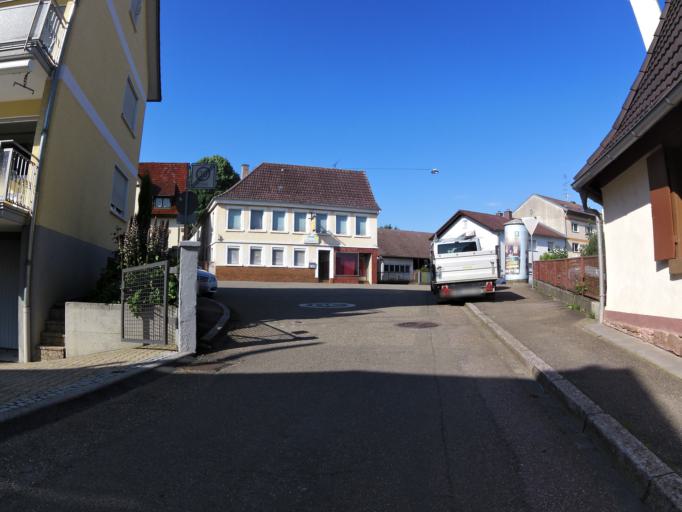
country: DE
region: Baden-Wuerttemberg
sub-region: Freiburg Region
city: Lahr
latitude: 48.3410
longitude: 7.8535
